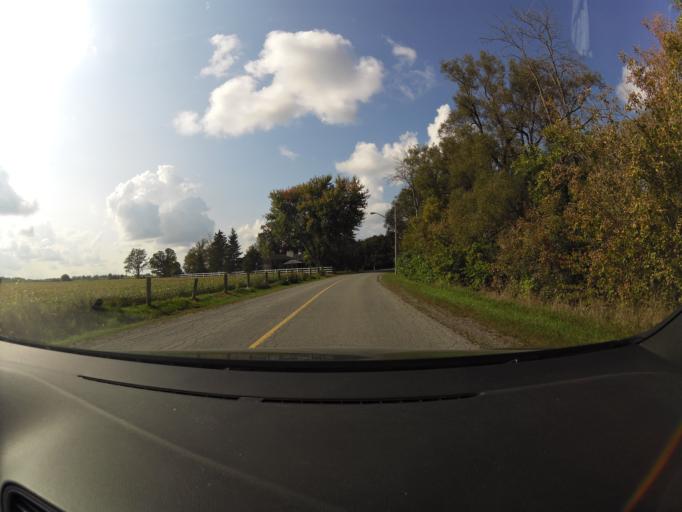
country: CA
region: Ontario
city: Arnprior
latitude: 45.3945
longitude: -76.1937
